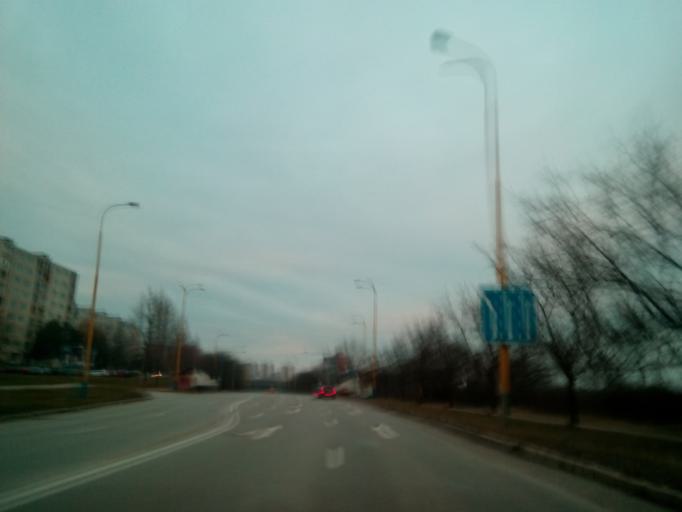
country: SK
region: Kosicky
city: Kosice
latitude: 48.7085
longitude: 21.2190
